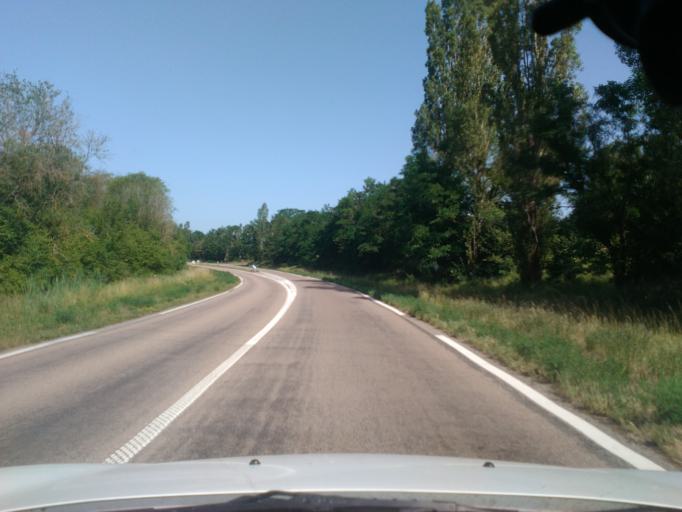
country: FR
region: Lorraine
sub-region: Departement des Vosges
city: Mirecourt
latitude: 48.3102
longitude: 6.0269
